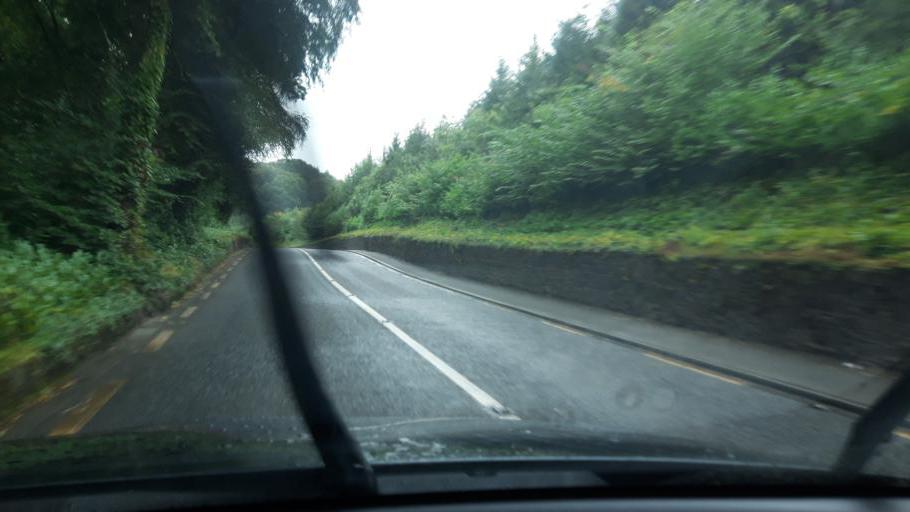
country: IE
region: Munster
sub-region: County Cork
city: Youghal
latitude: 52.1456
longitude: -7.9137
